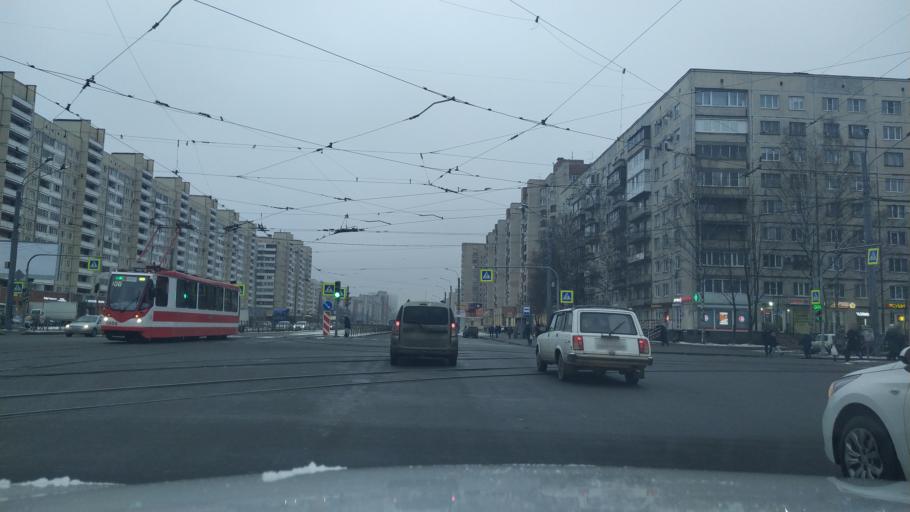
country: RU
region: St.-Petersburg
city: Grazhdanka
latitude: 60.0398
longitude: 30.3993
